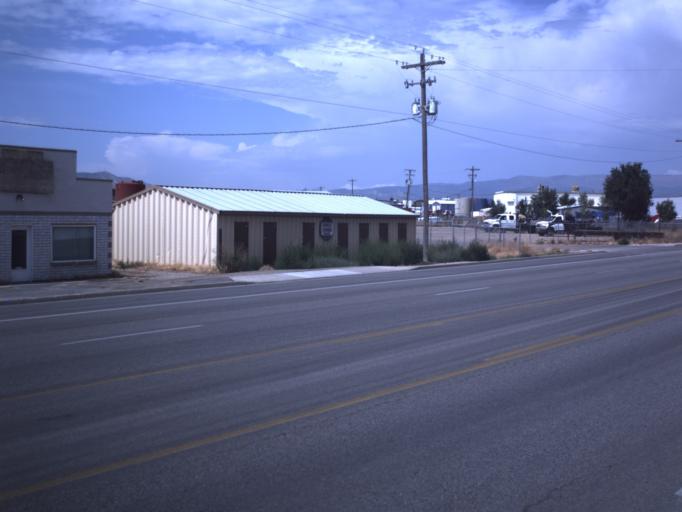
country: US
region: Utah
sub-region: Uintah County
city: Naples
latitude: 40.4501
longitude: -109.5034
